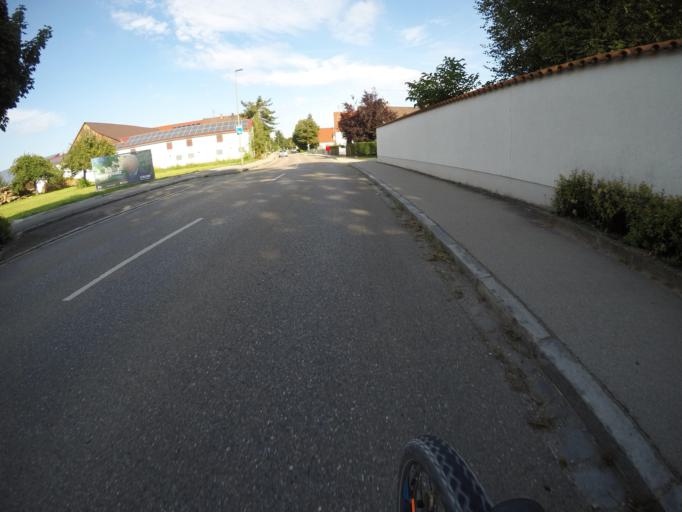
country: DE
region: Bavaria
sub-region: Swabia
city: Nordendorf
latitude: 48.5955
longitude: 10.8311
